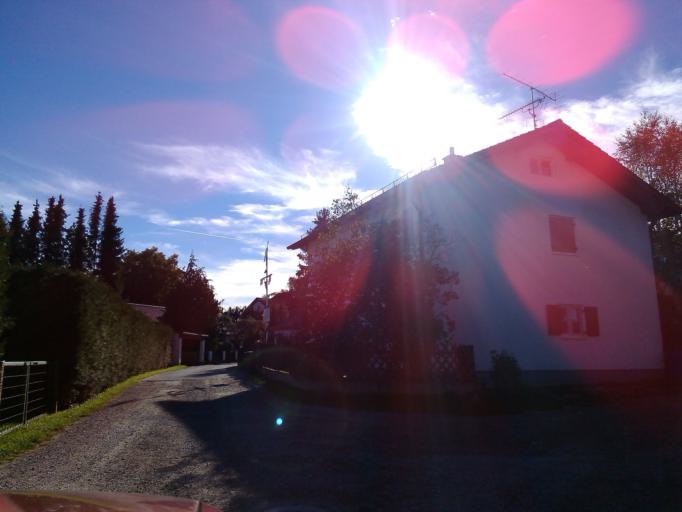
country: DE
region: Bavaria
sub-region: Upper Bavaria
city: Seefeld
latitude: 48.0306
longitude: 11.2546
